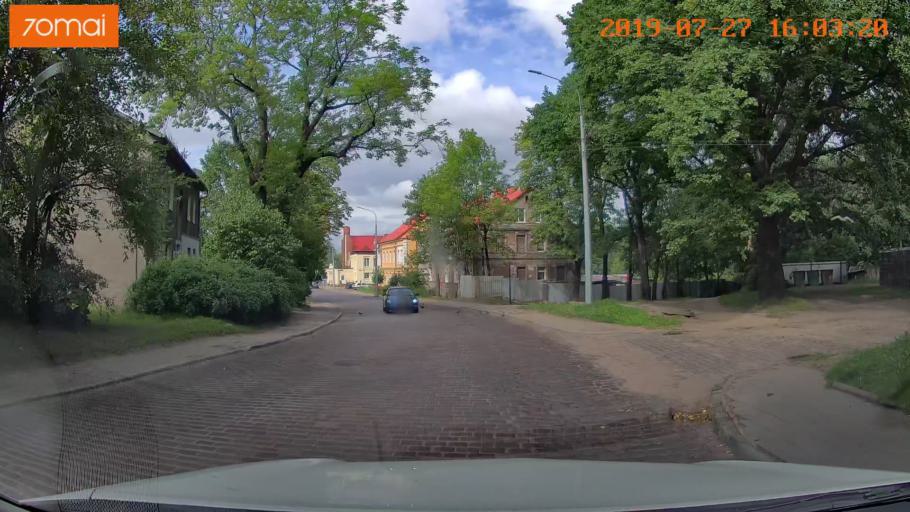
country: RU
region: Kaliningrad
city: Chernyakhovsk
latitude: 54.6319
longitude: 21.8030
